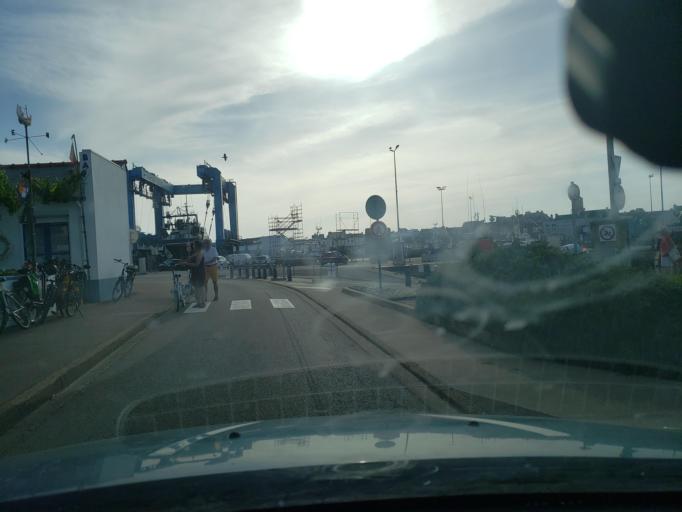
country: FR
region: Brittany
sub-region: Departement du Finistere
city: Guilvinec
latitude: 47.7937
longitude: -4.2785
